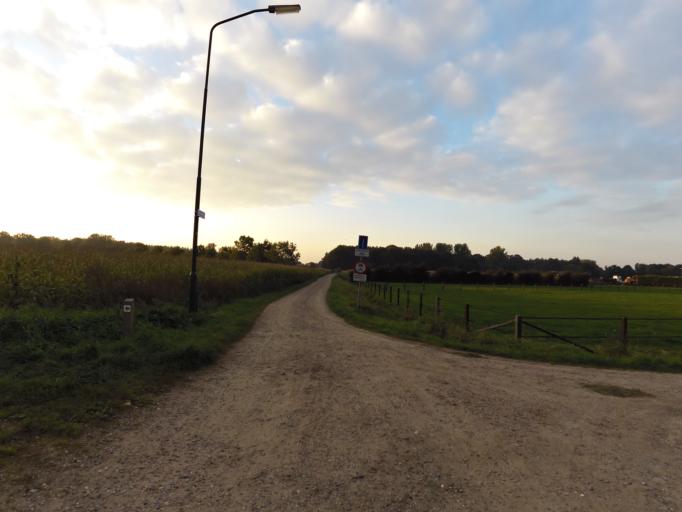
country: NL
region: Gelderland
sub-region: Gemeente Doesburg
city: Doesburg
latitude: 51.9532
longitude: 6.1997
